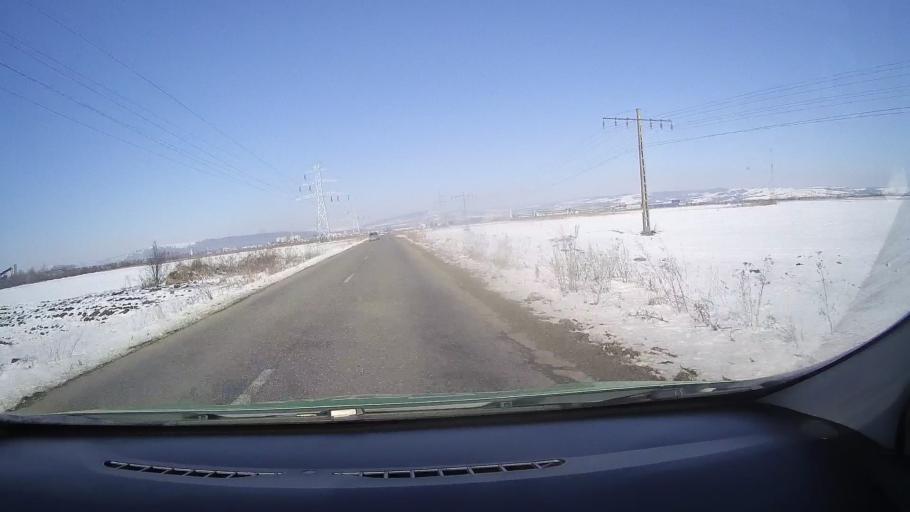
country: RO
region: Brasov
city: Fogarasch
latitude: 45.8126
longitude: 24.9888
